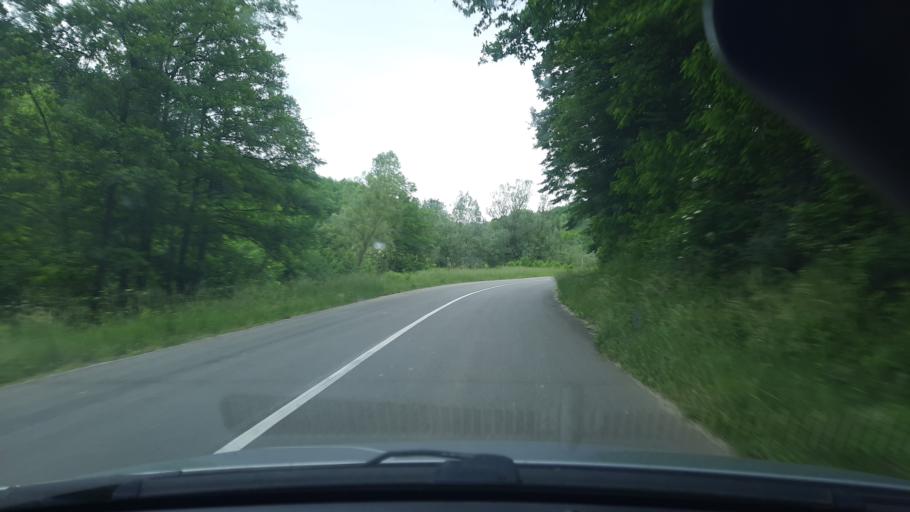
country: RS
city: Bukor
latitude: 44.5059
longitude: 19.4979
